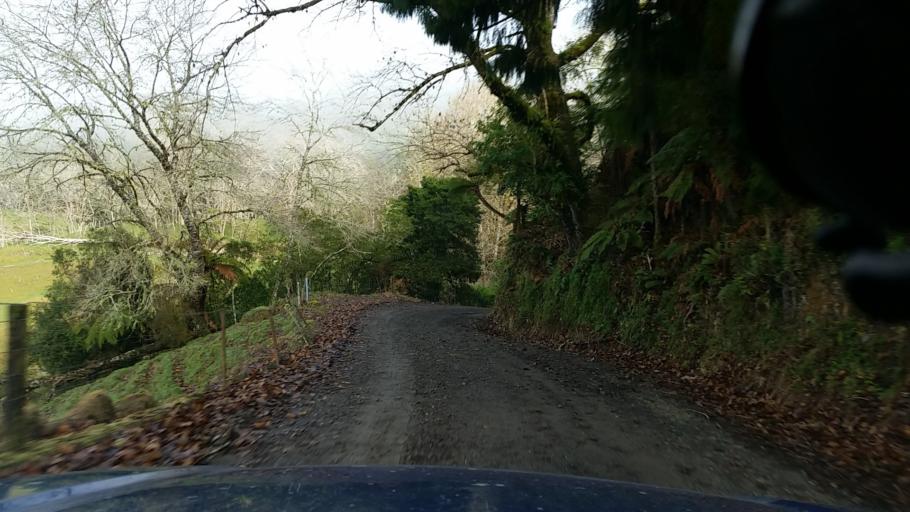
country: NZ
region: Taranaki
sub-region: New Plymouth District
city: Waitara
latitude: -39.0008
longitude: 174.7671
